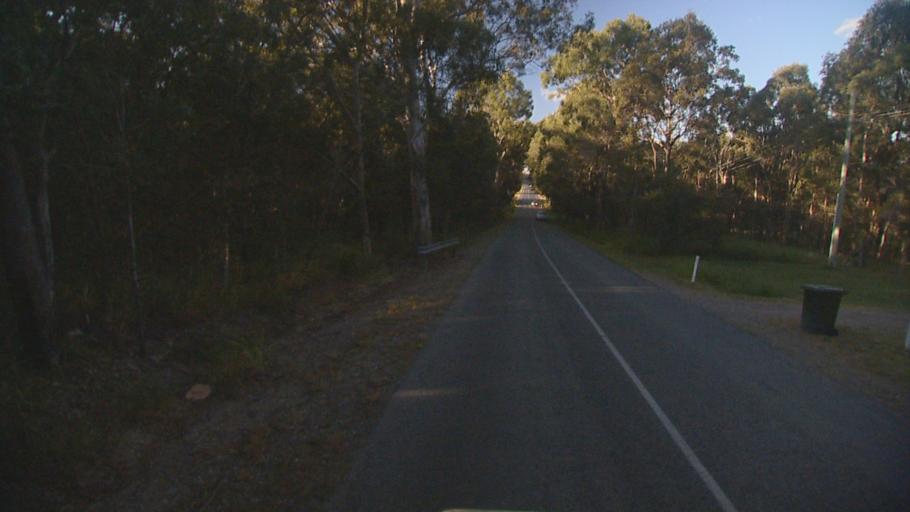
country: AU
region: Queensland
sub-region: Logan
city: Logan Reserve
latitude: -27.7228
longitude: 153.1072
